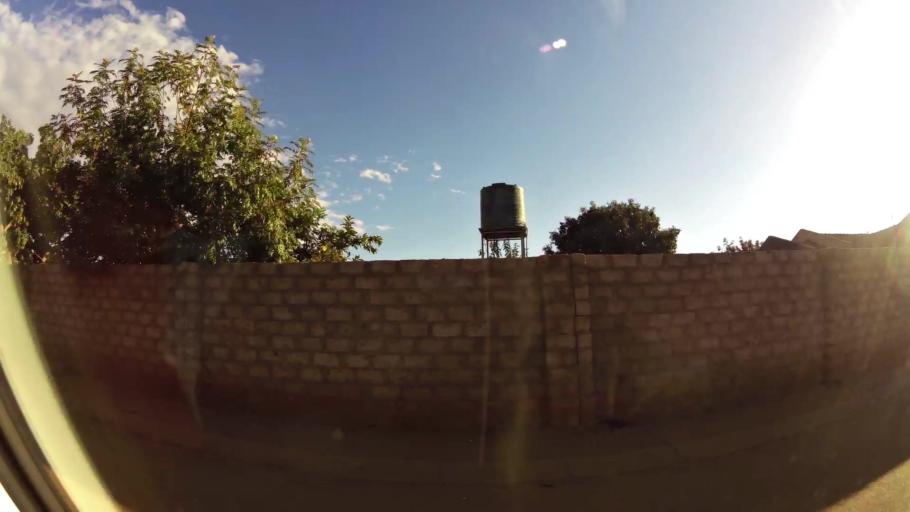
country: ZA
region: Limpopo
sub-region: Waterberg District Municipality
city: Mokopane
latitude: -24.1623
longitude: 28.9882
